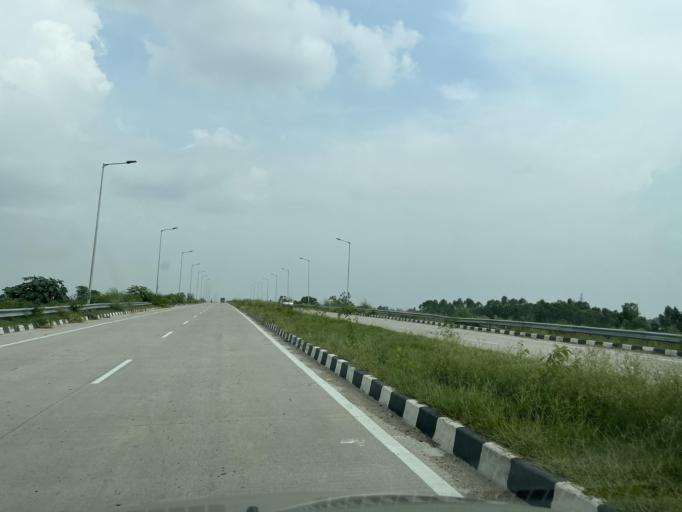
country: IN
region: Uttarakhand
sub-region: Udham Singh Nagar
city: Kashipur
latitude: 29.1753
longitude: 78.9431
